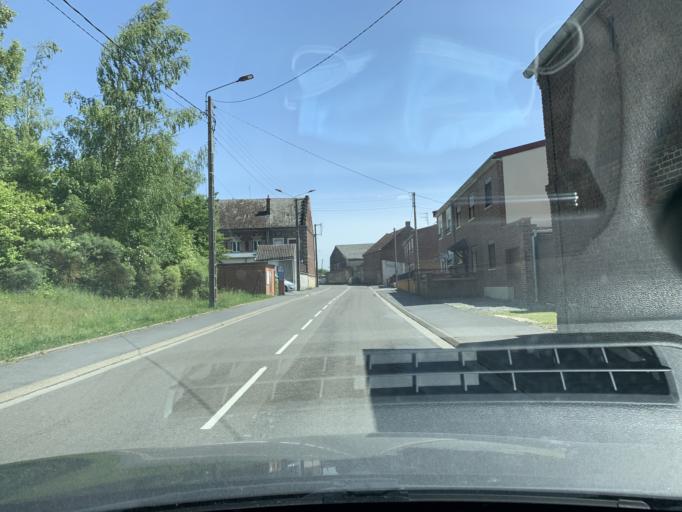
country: FR
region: Nord-Pas-de-Calais
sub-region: Departement du Nord
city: Masnieres
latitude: 50.1181
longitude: 3.2034
